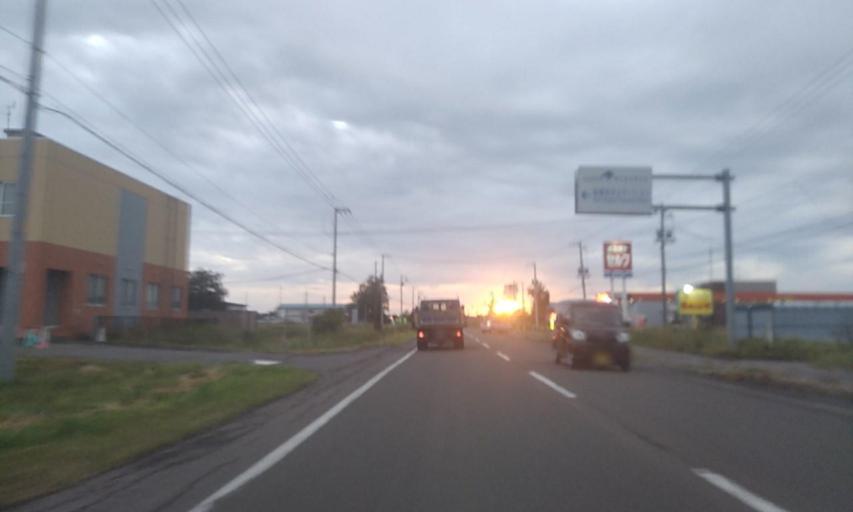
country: JP
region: Hokkaido
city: Abashiri
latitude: 43.9003
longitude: 144.6516
